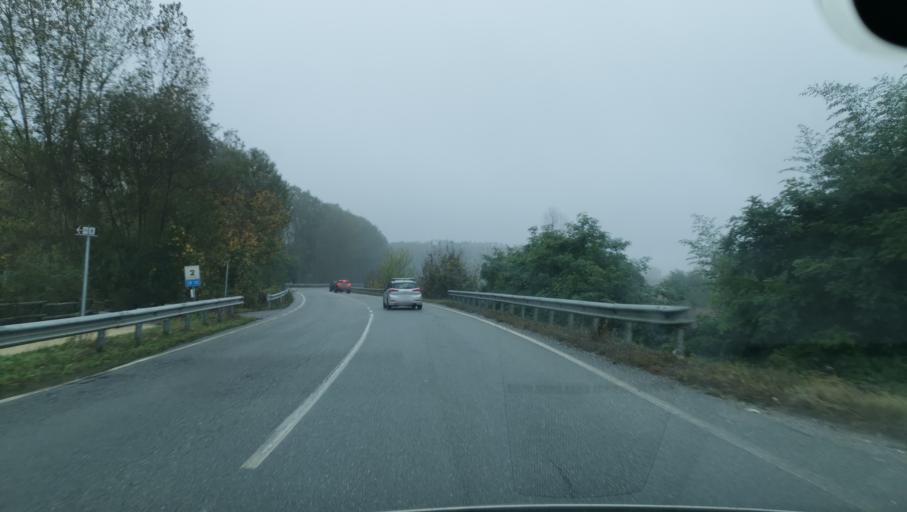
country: IT
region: Piedmont
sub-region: Provincia di Torino
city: Castiglione Torinese
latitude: 45.1257
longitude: 7.7886
